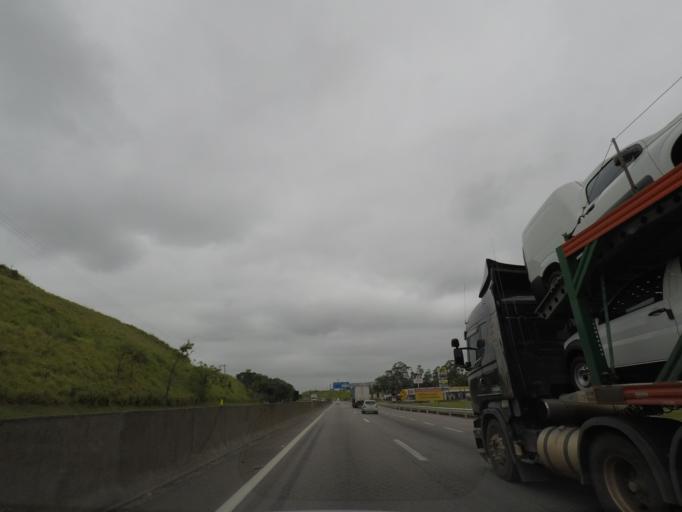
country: BR
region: Sao Paulo
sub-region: Jacarei
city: Jacarei
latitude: -23.3009
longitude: -46.0189
